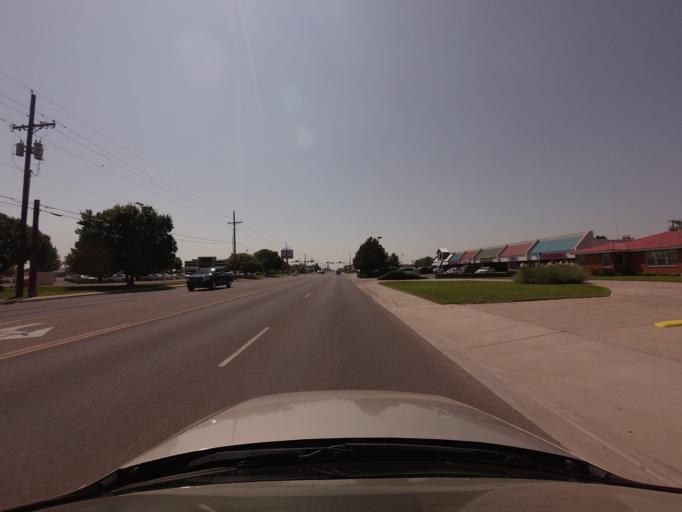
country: US
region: New Mexico
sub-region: Curry County
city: Clovis
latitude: 34.4255
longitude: -103.1966
